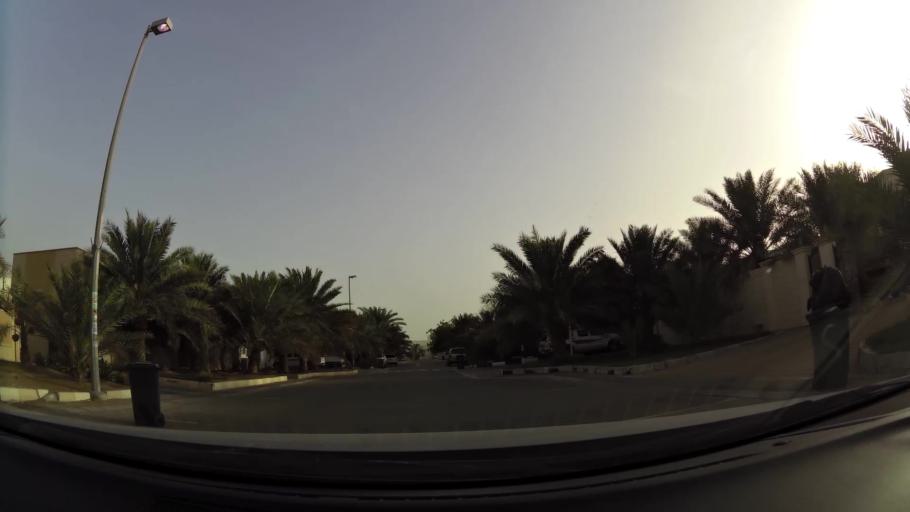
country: AE
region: Abu Dhabi
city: Al Ain
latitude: 24.1180
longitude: 55.7127
